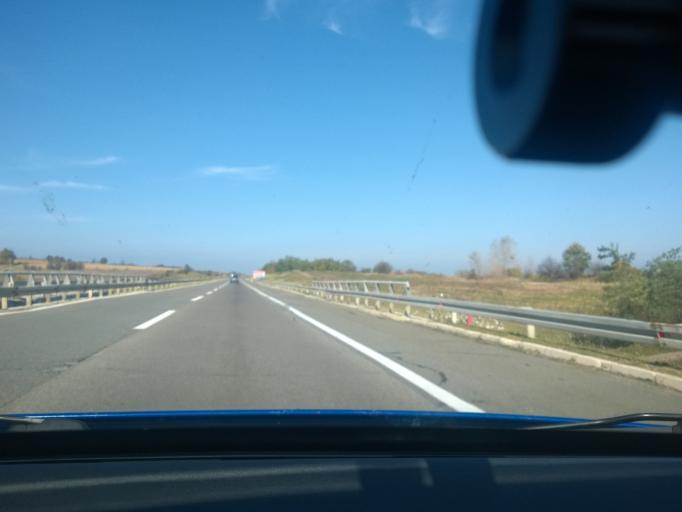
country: RS
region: Central Serbia
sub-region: Nisavski Okrug
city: Razanj
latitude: 43.7038
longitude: 21.5384
